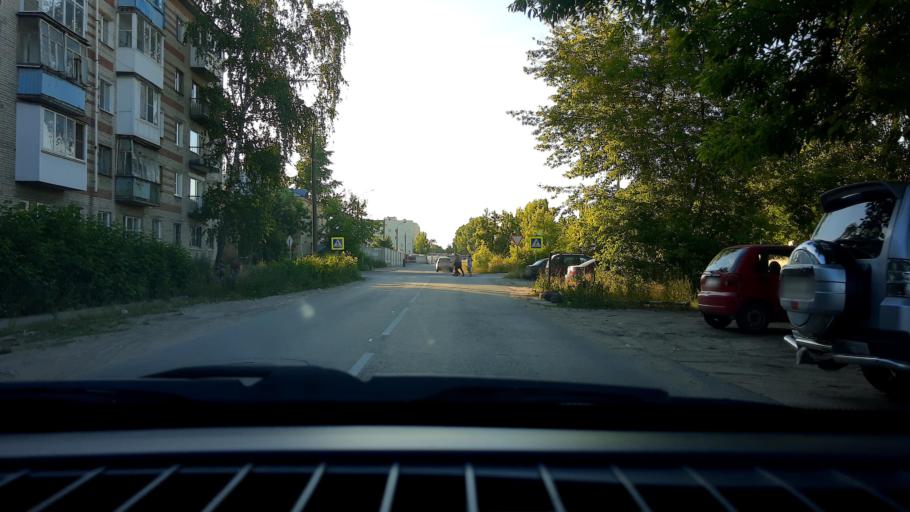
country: RU
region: Nizjnij Novgorod
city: Dzerzhinsk
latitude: 56.2421
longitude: 43.4866
